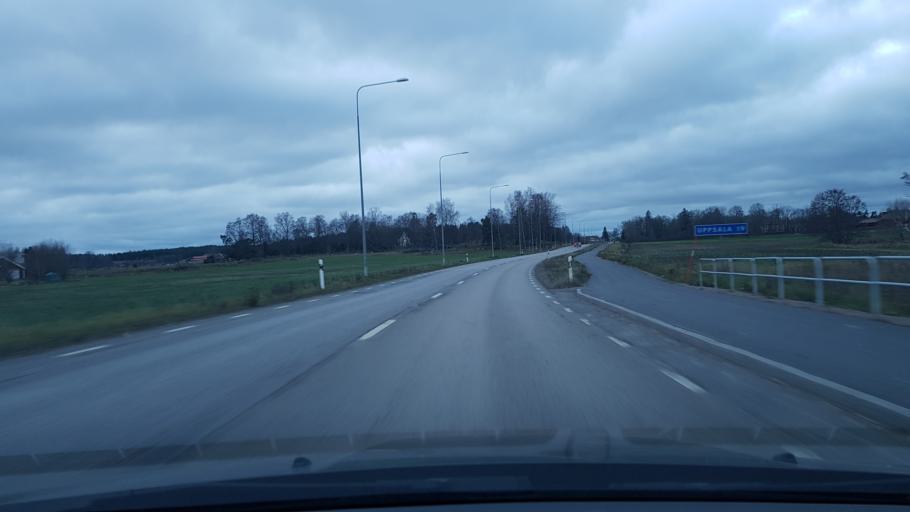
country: SE
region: Uppsala
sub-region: Uppsala Kommun
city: Vattholma
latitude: 59.9518
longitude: 17.8925
